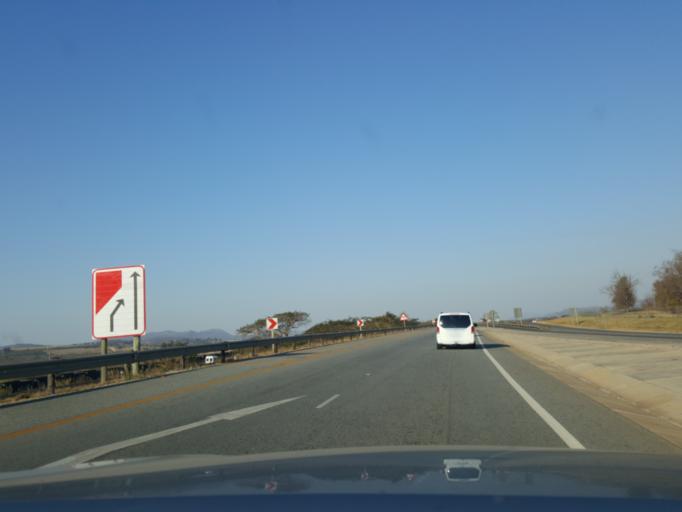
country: ZA
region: Mpumalanga
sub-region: Ehlanzeni District
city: Nelspruit
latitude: -25.4459
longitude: 30.9146
